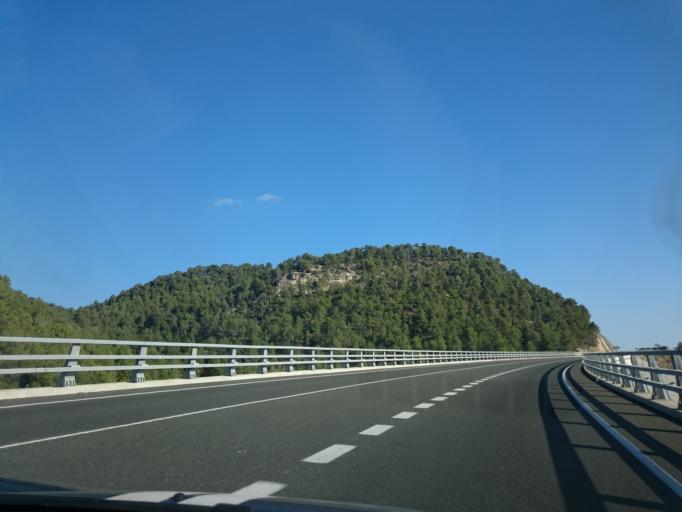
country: ES
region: Catalonia
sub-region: Provincia de Barcelona
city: Castelloli
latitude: 41.6079
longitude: 1.6772
